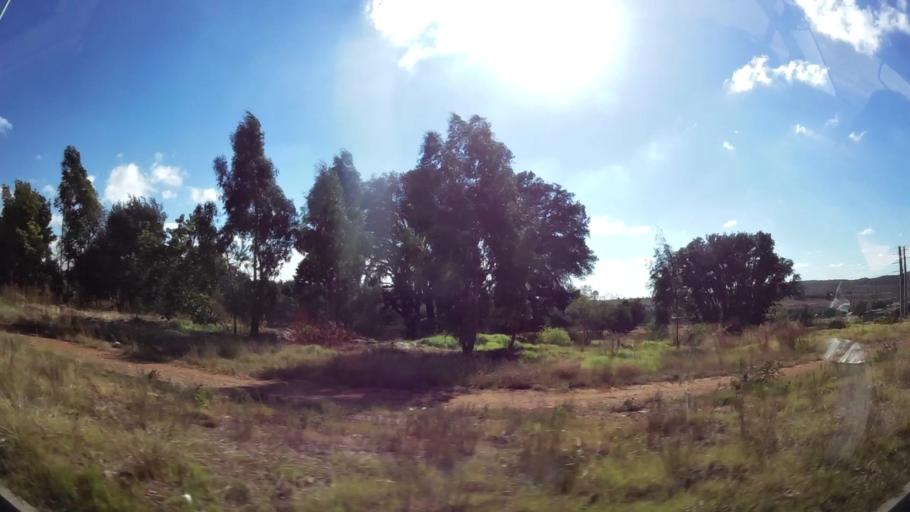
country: ZA
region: Gauteng
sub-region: West Rand District Municipality
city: Krugersdorp
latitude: -26.0865
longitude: 27.8104
